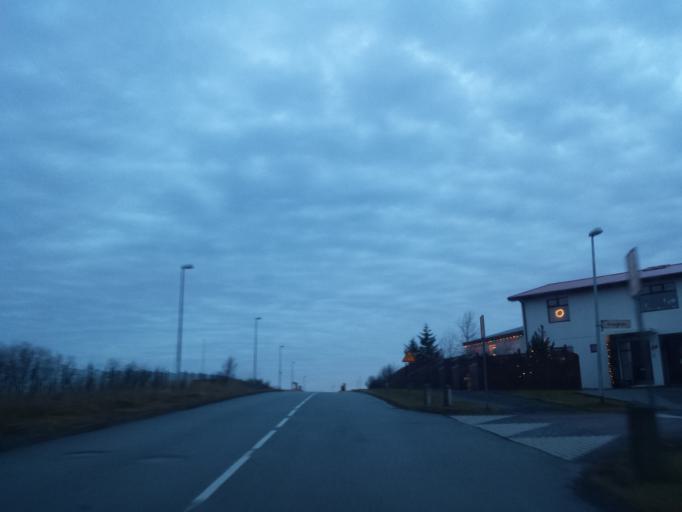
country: IS
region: Capital Region
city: Mosfellsbaer
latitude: 64.1368
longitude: -21.7710
